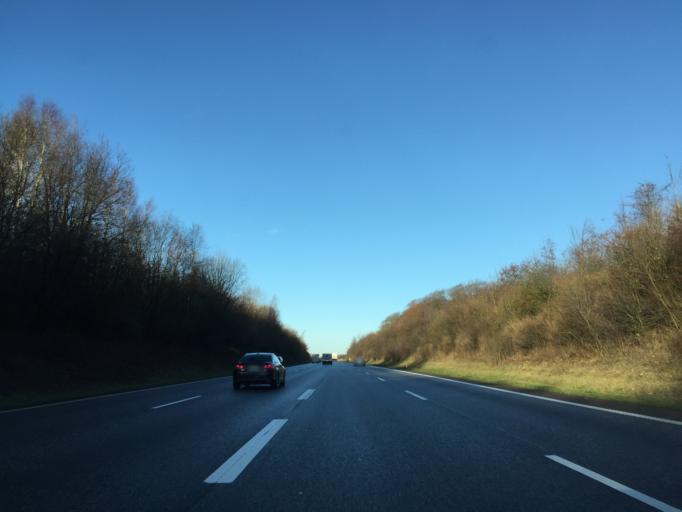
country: DK
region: South Denmark
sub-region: Fredericia Kommune
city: Taulov
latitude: 55.6044
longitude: 9.5861
